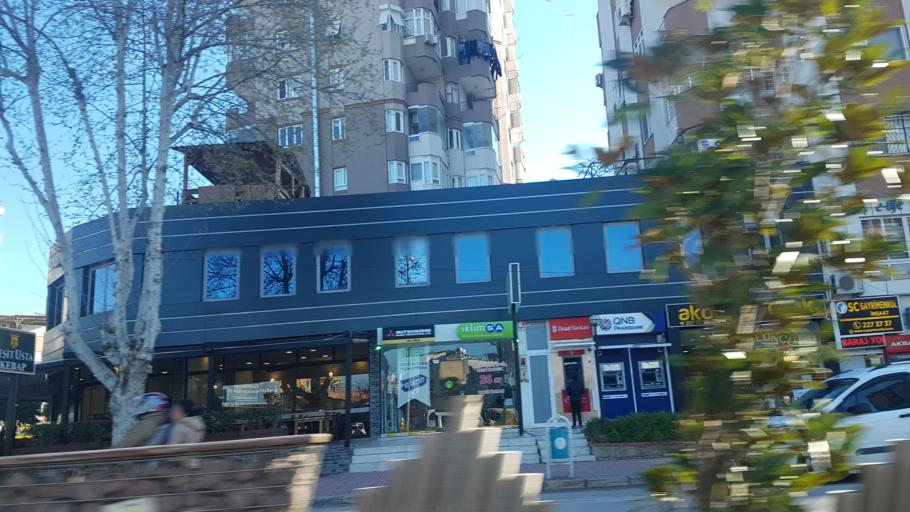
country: TR
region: Adana
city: Adana
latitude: 37.0178
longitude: 35.3176
